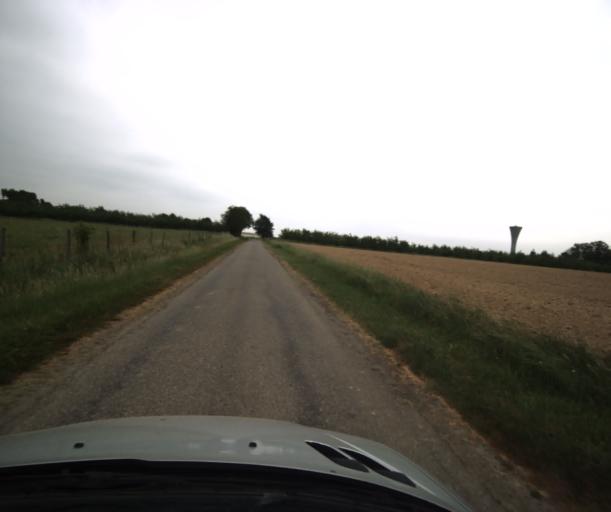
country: FR
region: Midi-Pyrenees
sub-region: Departement du Tarn-et-Garonne
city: Saint-Nicolas-de-la-Grave
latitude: 44.0536
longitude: 0.9997
